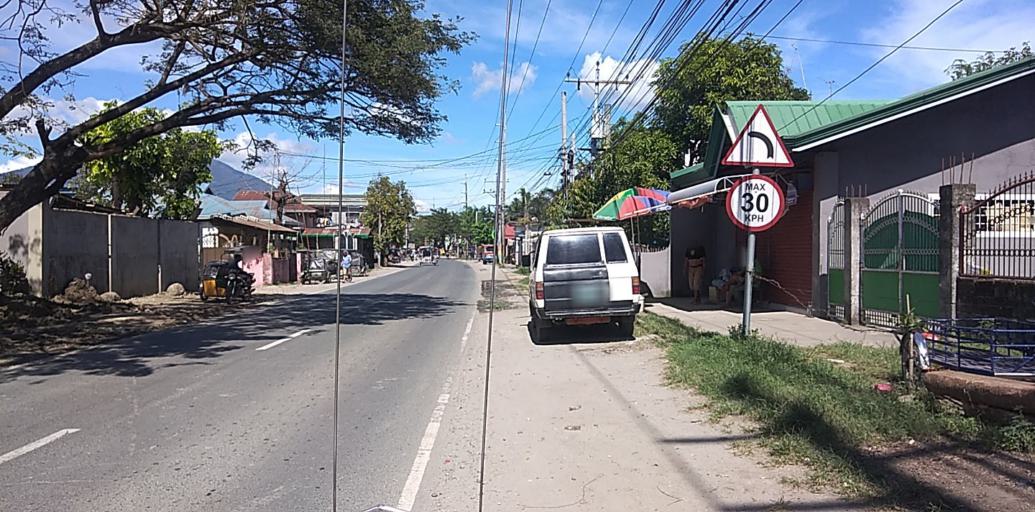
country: PH
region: Central Luzon
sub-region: Province of Pampanga
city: Arayat
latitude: 15.1256
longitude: 120.7758
